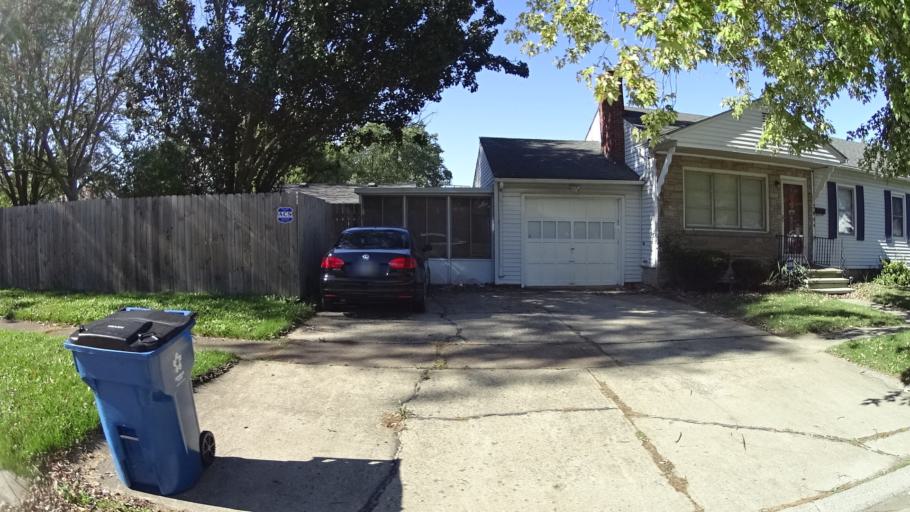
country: US
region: Ohio
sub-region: Lorain County
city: Lorain
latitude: 41.4446
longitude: -82.1824
